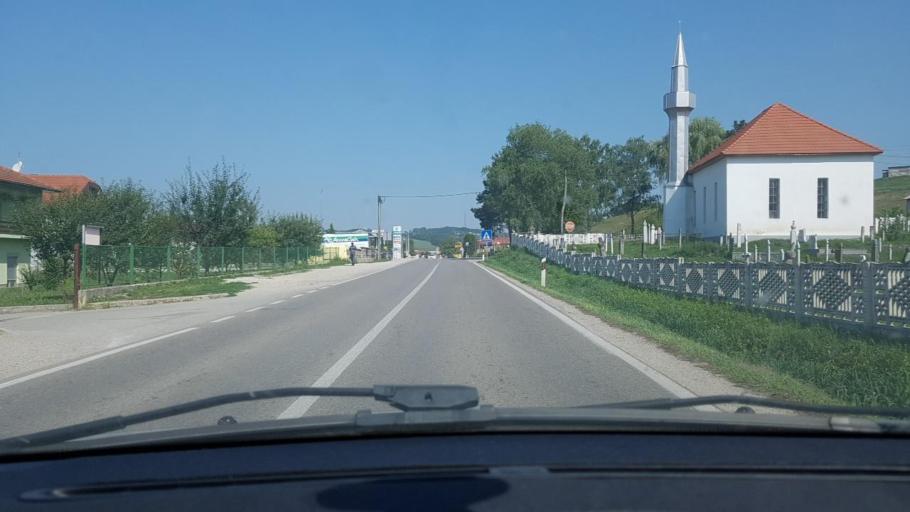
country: BA
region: Federation of Bosnia and Herzegovina
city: Velika Kladusa
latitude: 45.1588
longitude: 15.8231
